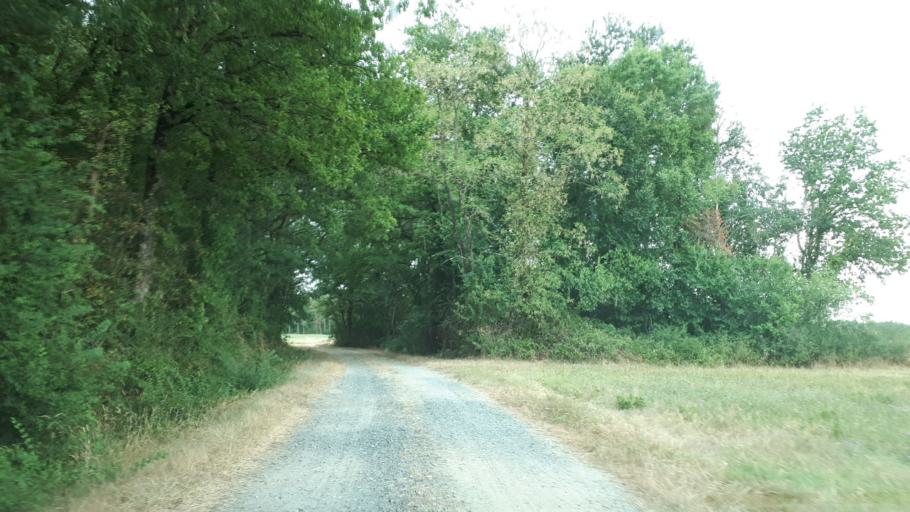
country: FR
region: Centre
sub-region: Departement du Loir-et-Cher
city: Saint-Romain-sur-Cher
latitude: 47.3539
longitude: 1.3938
